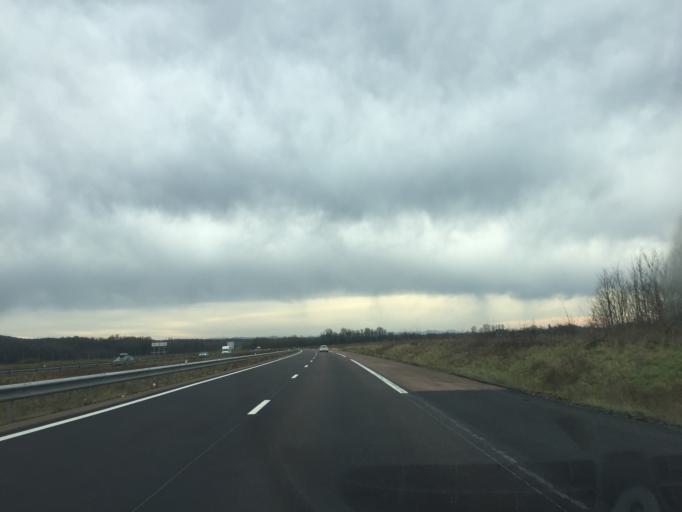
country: FR
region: Franche-Comte
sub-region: Departement du Jura
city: Bletterans
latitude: 46.7579
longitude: 5.5091
